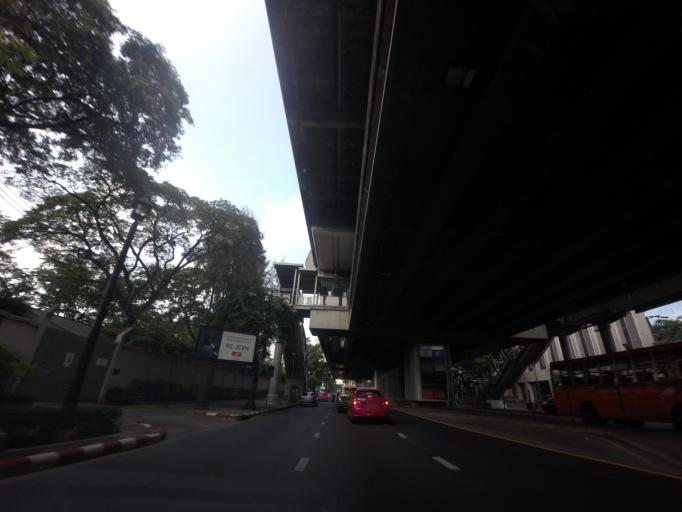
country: TH
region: Bangkok
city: Pathum Wan
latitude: 13.7389
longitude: 100.5393
